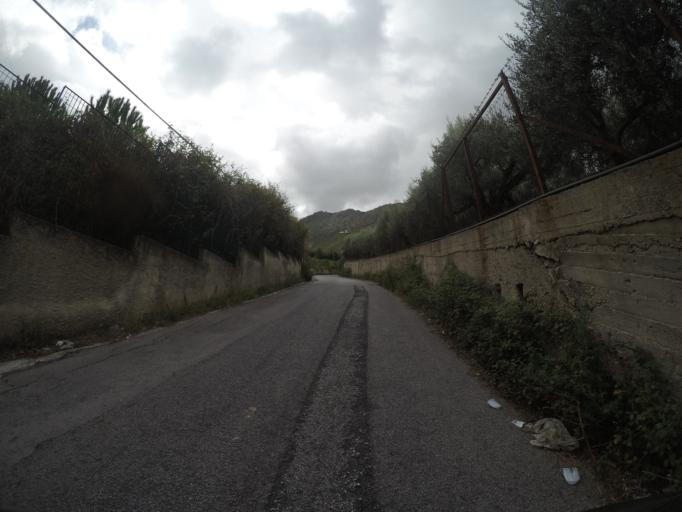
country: IT
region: Sicily
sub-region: Palermo
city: Carini
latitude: 38.1230
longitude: 13.1842
